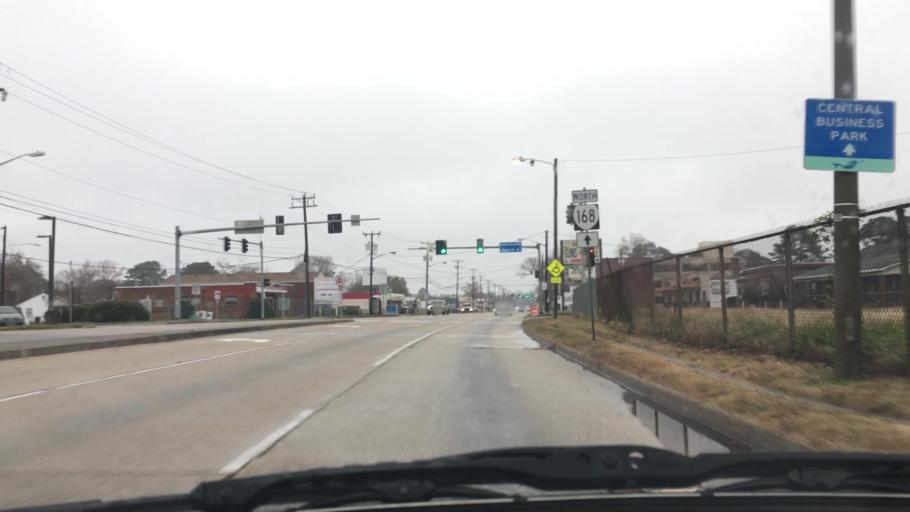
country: US
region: Virginia
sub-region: City of Norfolk
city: Norfolk
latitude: 36.9090
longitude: -76.2563
